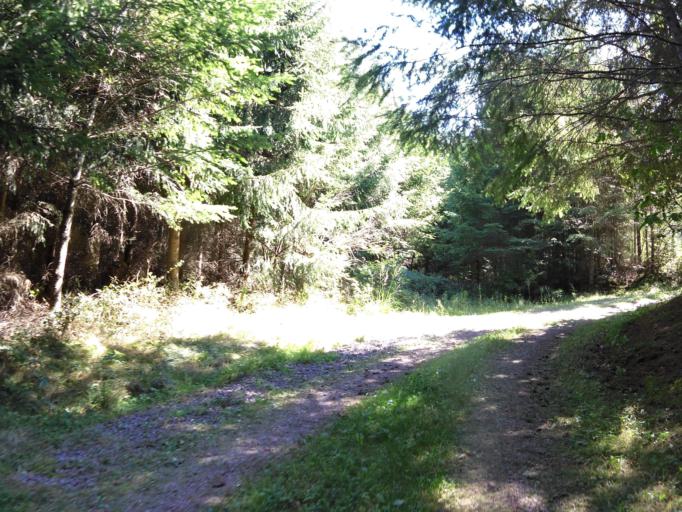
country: DE
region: Baden-Wuerttemberg
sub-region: Freiburg Region
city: Hohberg
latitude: 48.3332
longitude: 7.9002
